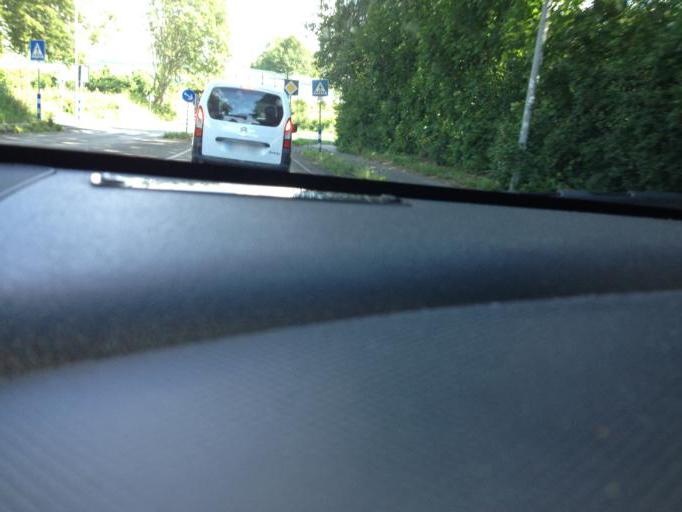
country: DE
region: North Rhine-Westphalia
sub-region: Regierungsbezirk Arnsberg
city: Holzwickede
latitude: 51.5279
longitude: 7.6513
